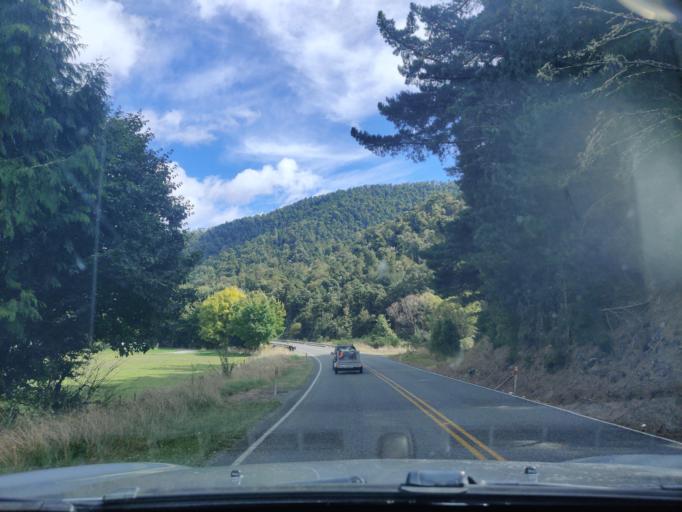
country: NZ
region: Tasman
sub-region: Tasman District
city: Wakefield
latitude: -41.6929
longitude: 172.4940
